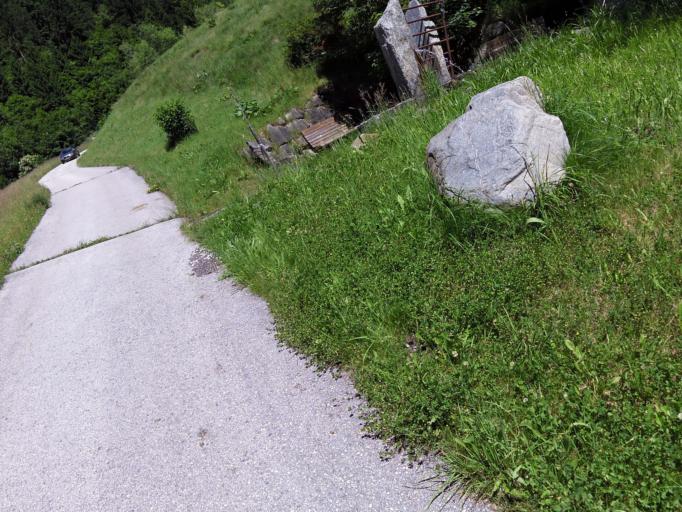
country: AT
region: Tyrol
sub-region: Politischer Bezirk Innsbruck Land
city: Neustift im Stubaital
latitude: 47.1119
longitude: 11.3017
